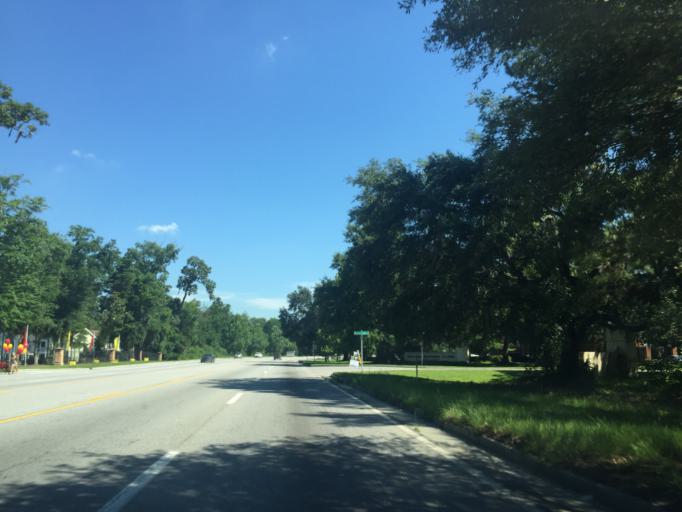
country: US
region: Georgia
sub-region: Chatham County
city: Garden City
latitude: 32.0510
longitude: -81.1664
